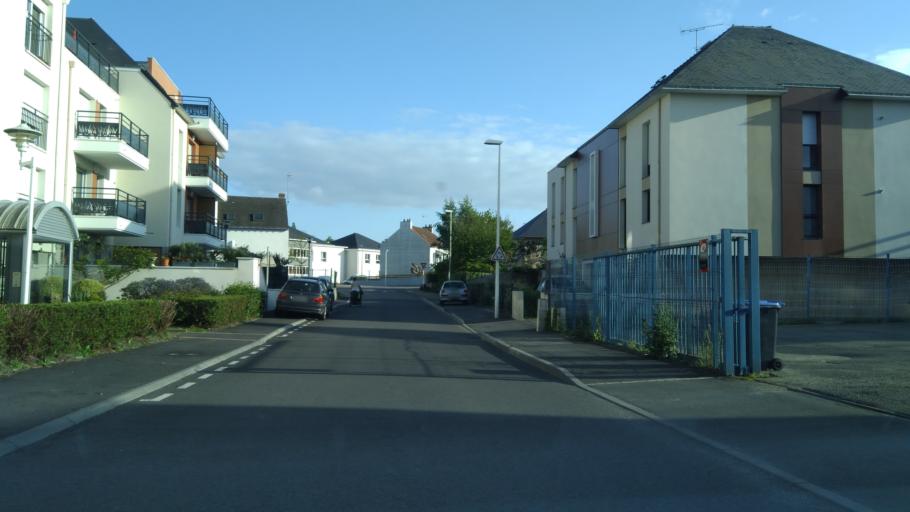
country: FR
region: Pays de la Loire
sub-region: Departement de la Loire-Atlantique
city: Pornichet
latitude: 47.2574
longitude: -2.3243
